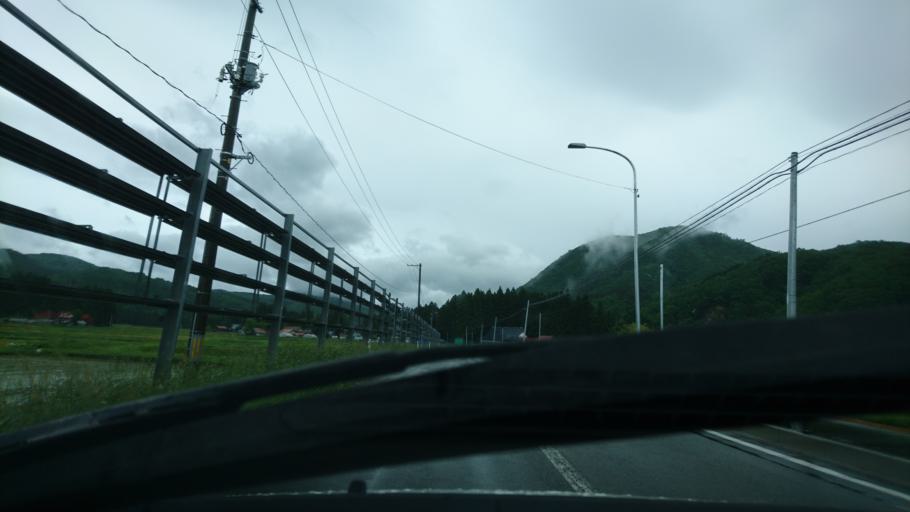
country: JP
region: Iwate
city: Ichinoseki
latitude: 38.9805
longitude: 140.9190
